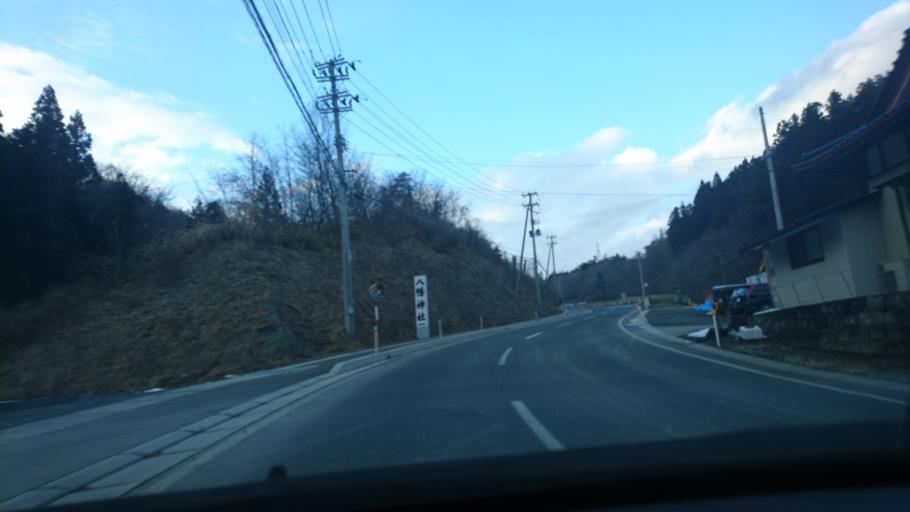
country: JP
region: Iwate
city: Ichinoseki
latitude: 38.9996
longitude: 141.3332
